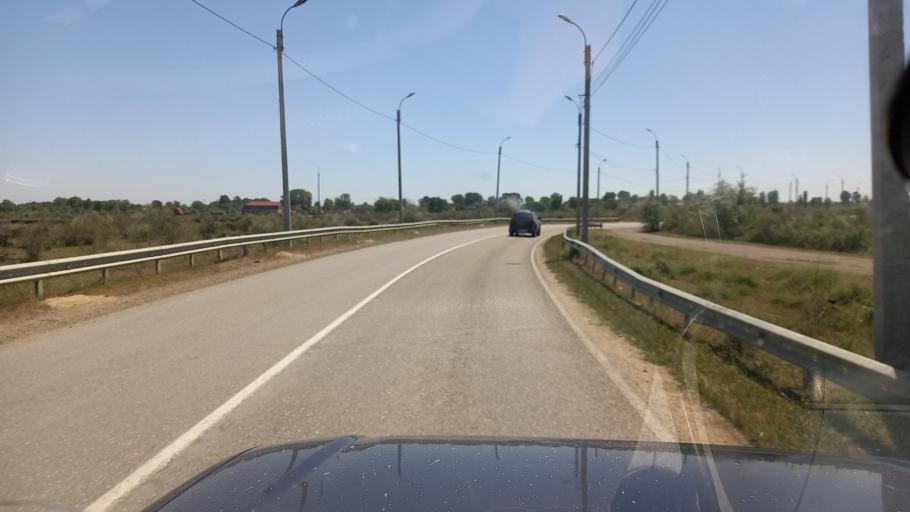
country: RU
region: Dagestan
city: Samur
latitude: 41.7360
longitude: 48.4507
